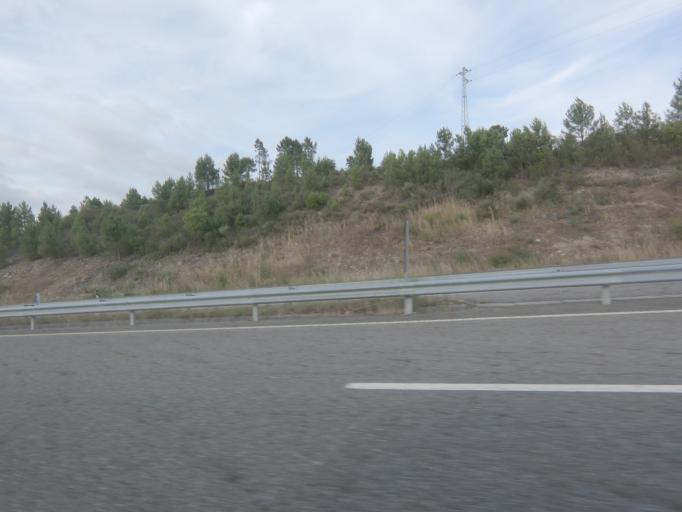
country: PT
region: Vila Real
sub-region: Boticas
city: Boticas
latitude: 41.6310
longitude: -7.5957
